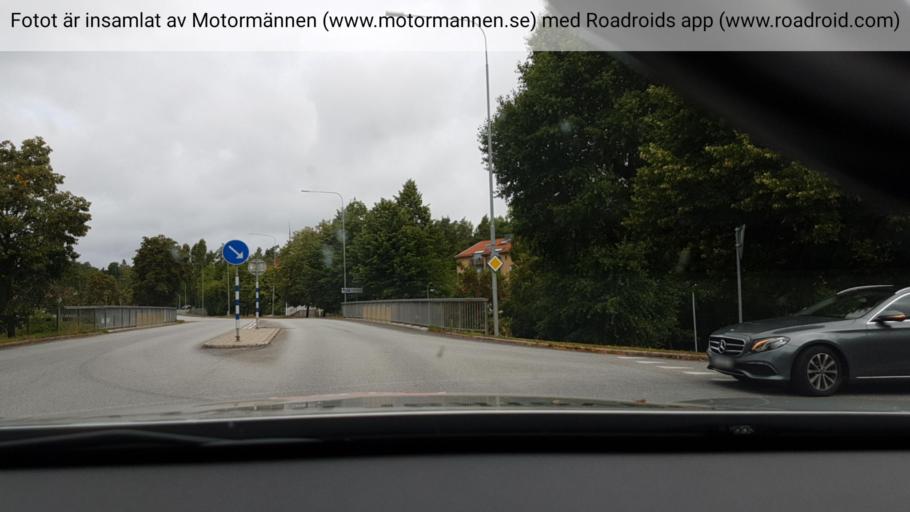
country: SE
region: Stockholm
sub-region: Lidingo
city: Lidingoe
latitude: 59.3659
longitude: 18.1374
